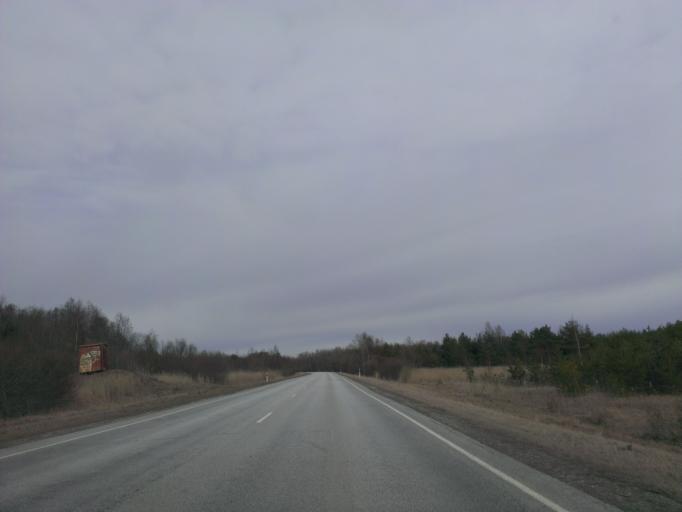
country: EE
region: Laeaene
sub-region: Lihula vald
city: Lihula
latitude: 58.5963
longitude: 23.5475
